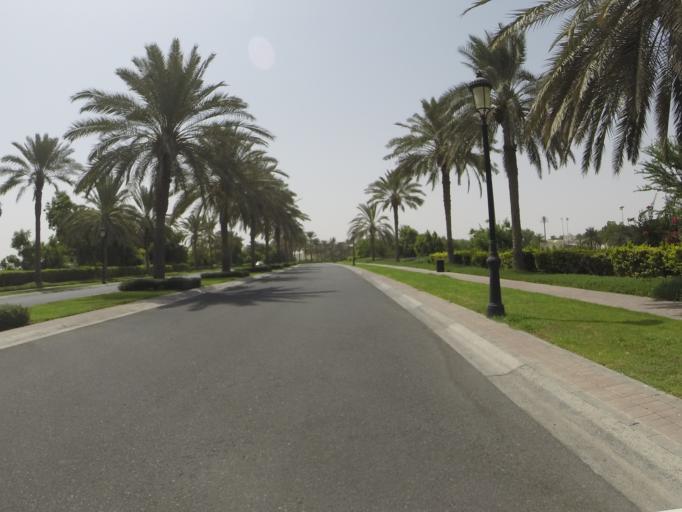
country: AE
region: Dubai
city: Dubai
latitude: 25.0702
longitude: 55.1606
